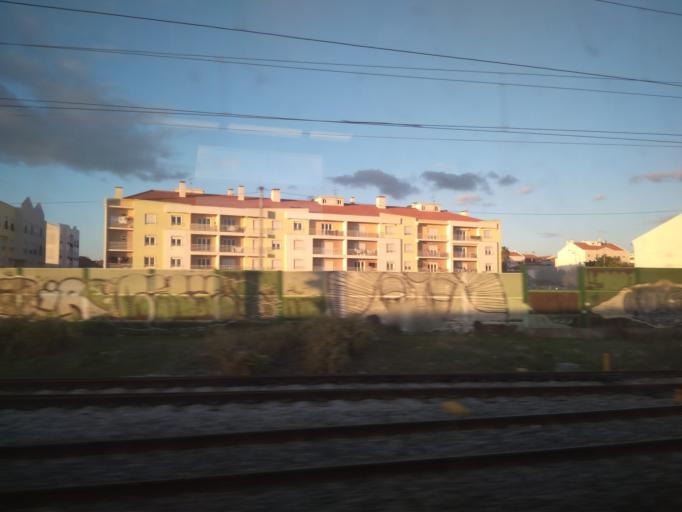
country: PT
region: Setubal
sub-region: Palmela
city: Pinhal Novo
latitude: 38.6300
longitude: -8.9187
